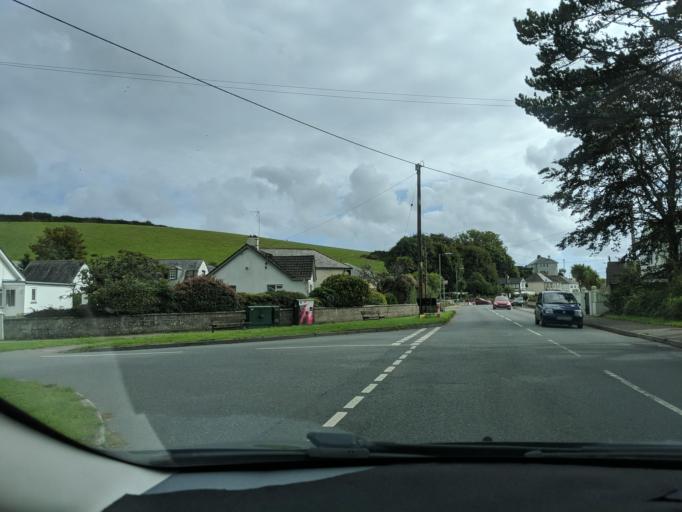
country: GB
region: England
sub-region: Cornwall
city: Par
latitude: 50.3547
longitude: -4.7010
